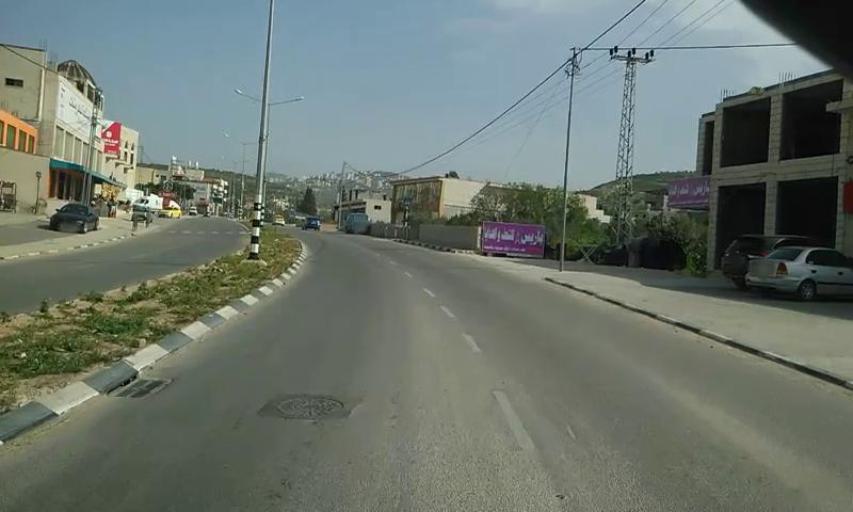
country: PS
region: West Bank
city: Dayr Sharaf
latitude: 32.2517
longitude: 35.1867
